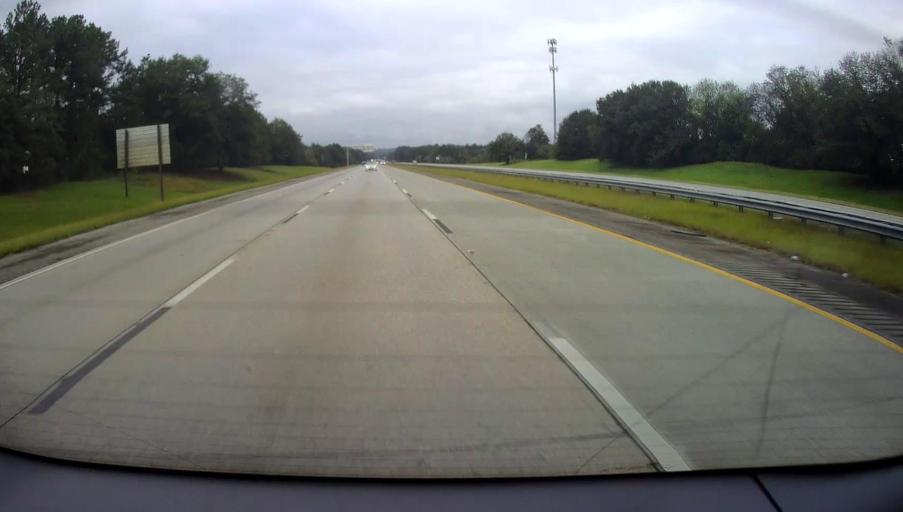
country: US
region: Georgia
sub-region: Bibb County
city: Macon
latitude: 32.7788
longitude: -83.6816
